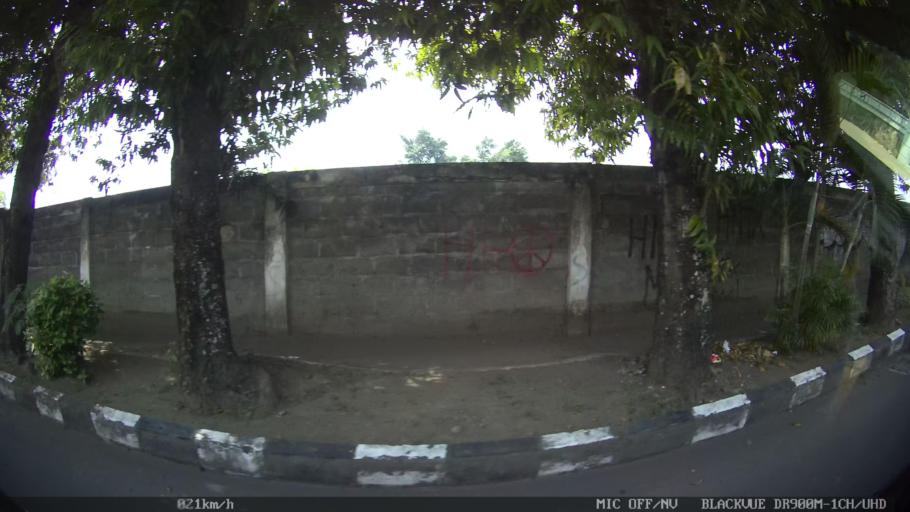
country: ID
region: Daerah Istimewa Yogyakarta
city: Yogyakarta
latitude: -7.7964
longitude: 110.3873
